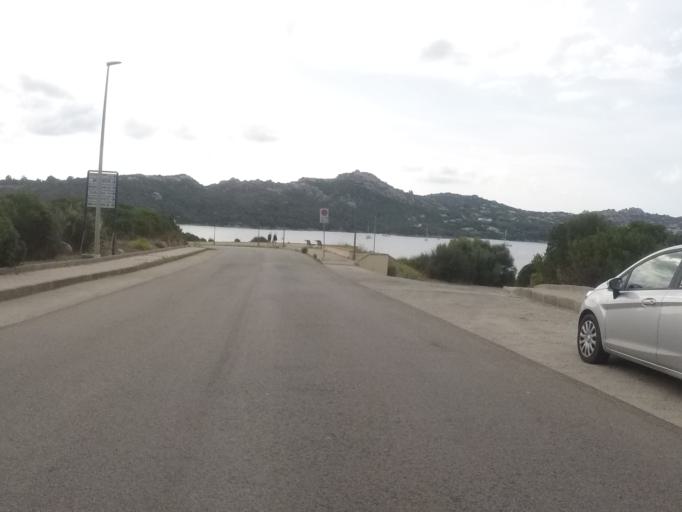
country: IT
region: Sardinia
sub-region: Provincia di Olbia-Tempio
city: Palau
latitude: 41.1847
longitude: 9.3782
